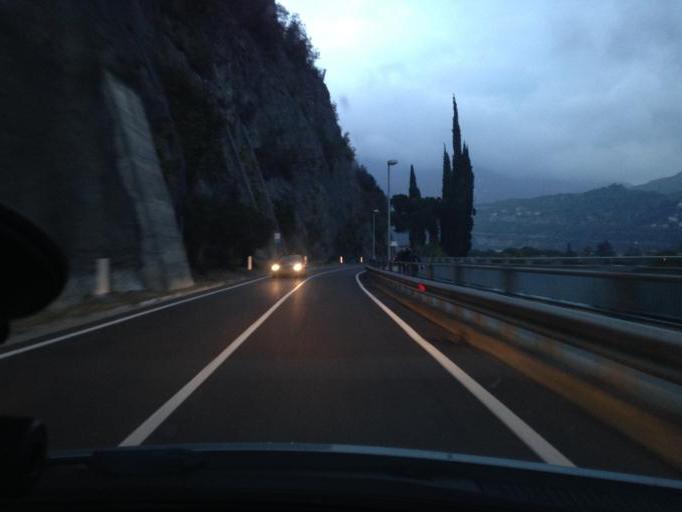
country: IT
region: Trentino-Alto Adige
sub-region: Provincia di Trento
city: Torbole sul Garda
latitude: 45.8766
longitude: 10.8599
